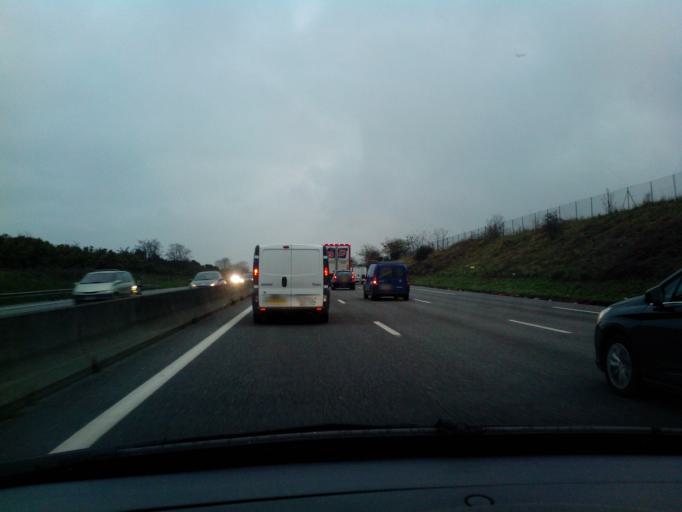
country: FR
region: Ile-de-France
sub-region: Departement de l'Essonne
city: Chilly-Mazarin
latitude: 48.7230
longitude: 2.3120
